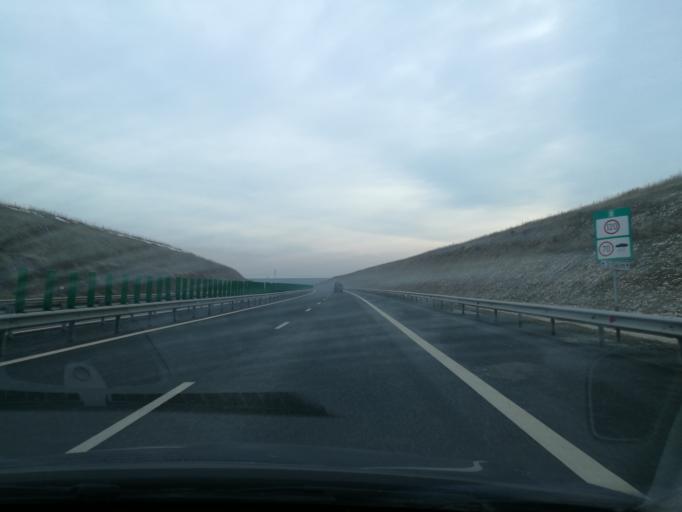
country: RO
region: Constanta
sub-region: Comuna Saligny
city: Saligny
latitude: 44.2431
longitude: 28.0942
